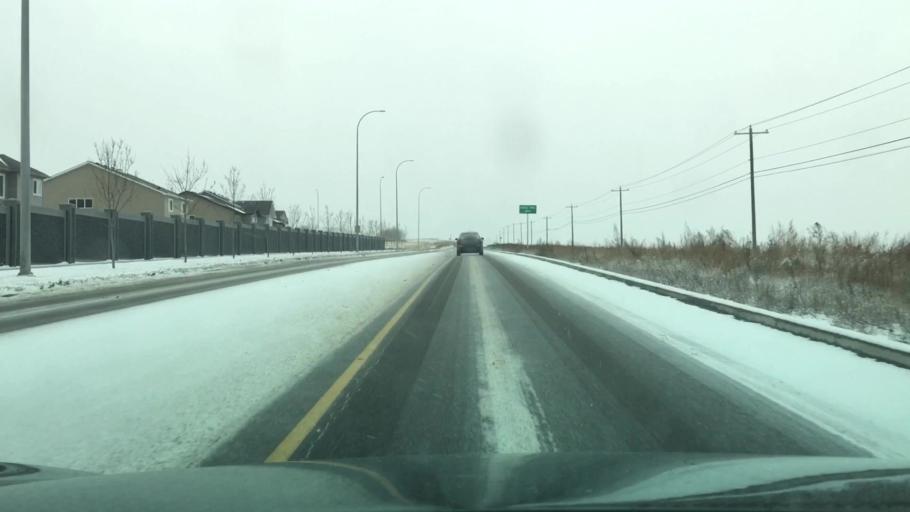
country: CA
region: Alberta
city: Calgary
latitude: 51.1831
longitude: -114.1732
